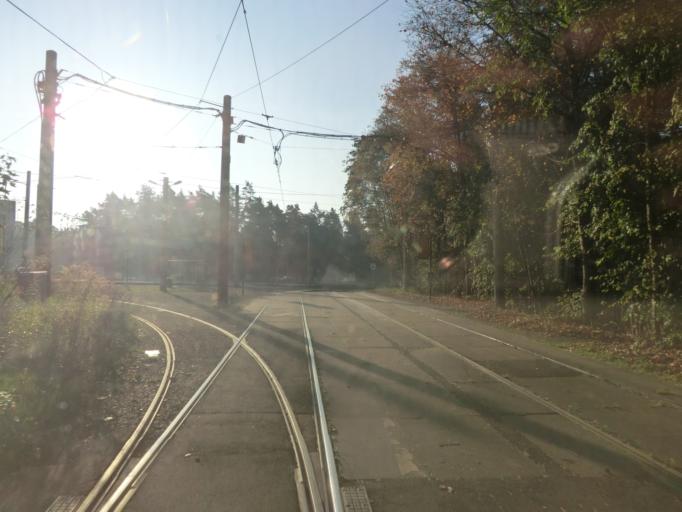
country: DE
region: Saxony
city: Albertstadt
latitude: 51.1032
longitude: 13.7697
